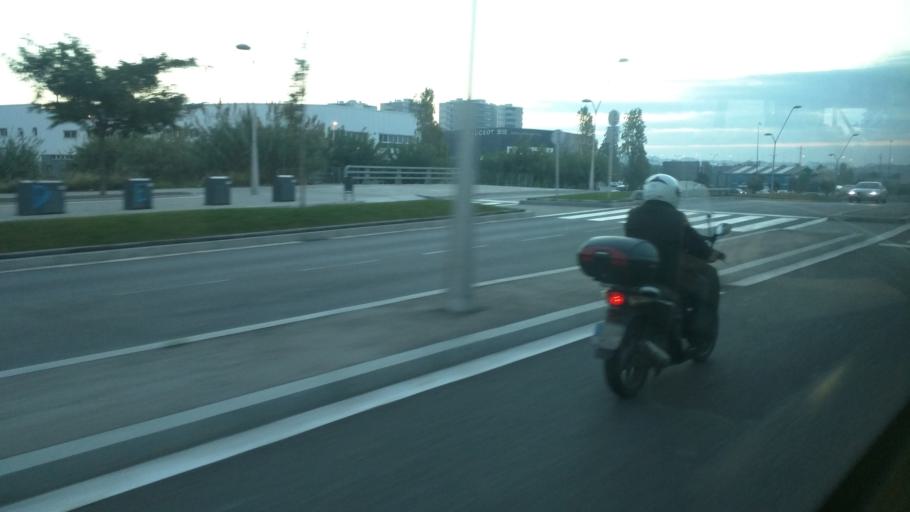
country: ES
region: Catalonia
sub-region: Provincia de Barcelona
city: Sant Feliu de Llobregat
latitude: 41.3755
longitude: 2.0417
